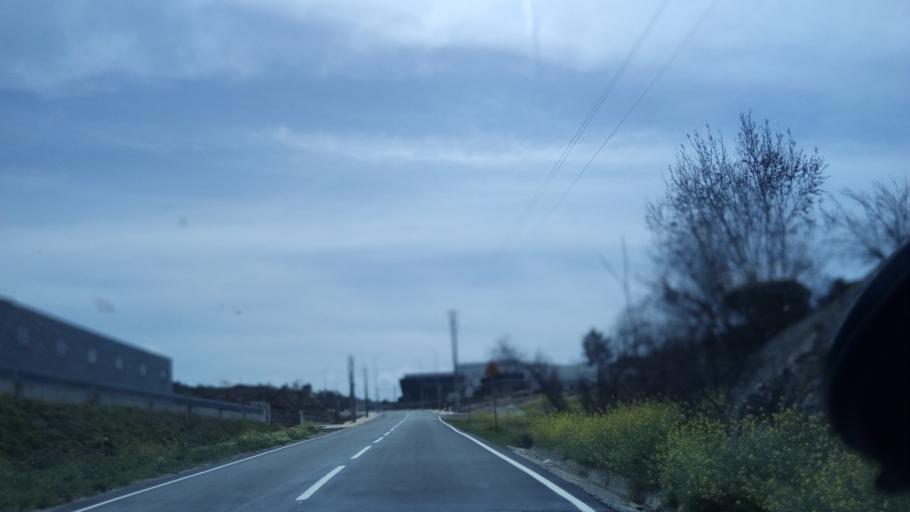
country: PT
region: Viseu
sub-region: Mangualde
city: Mangualde
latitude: 40.6104
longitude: -7.7887
